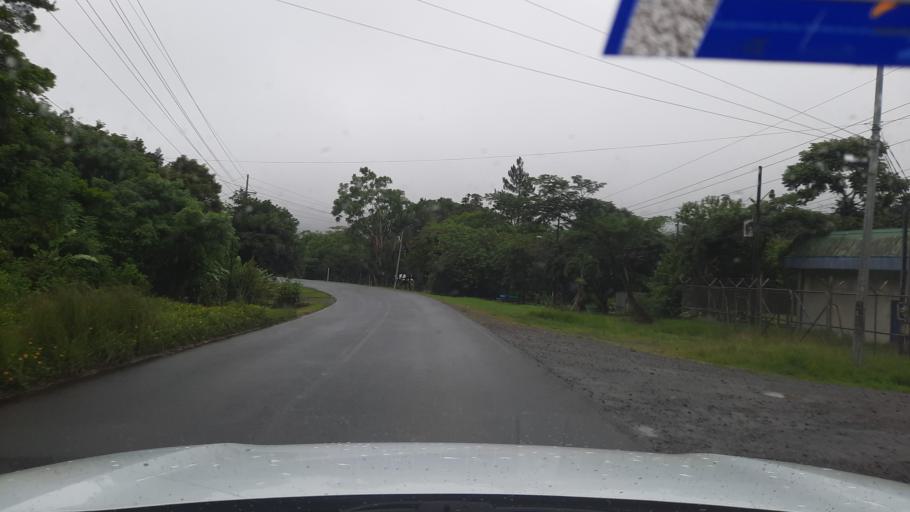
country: CR
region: Alajuela
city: Bijagua
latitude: 10.7282
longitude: -85.0632
